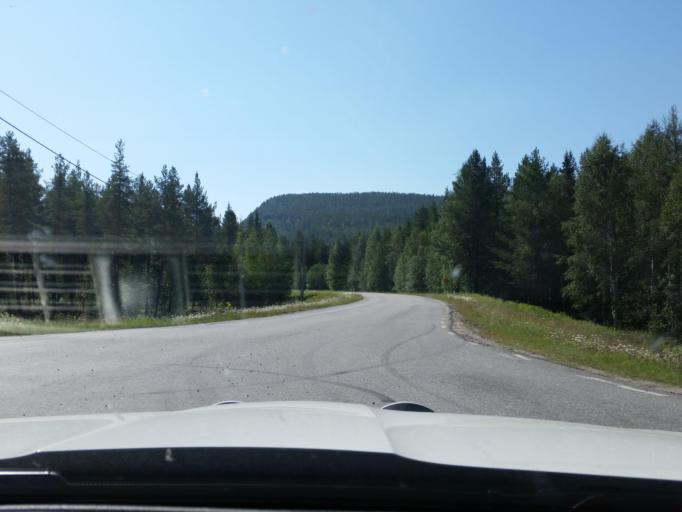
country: SE
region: Norrbotten
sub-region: Alvsbyns Kommun
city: AElvsbyn
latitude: 65.7464
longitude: 20.9271
